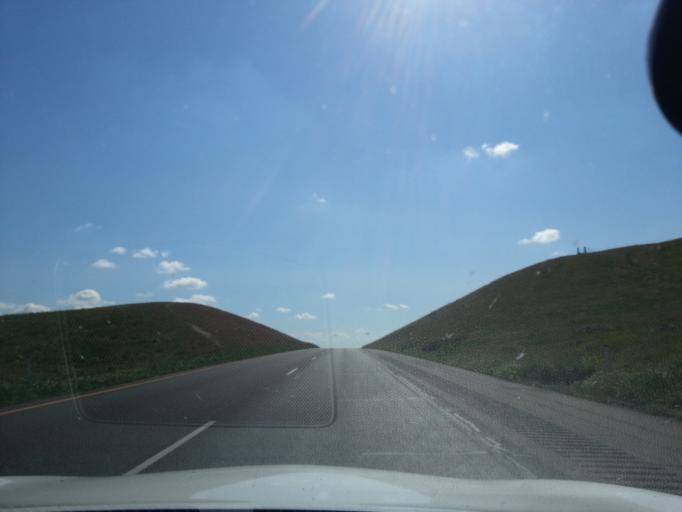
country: US
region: California
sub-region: Fresno County
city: Coalinga
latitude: 36.3229
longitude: -120.2937
